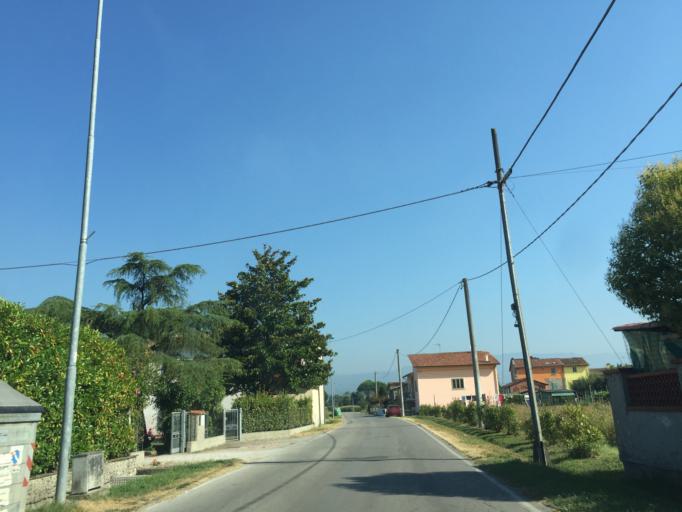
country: IT
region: Tuscany
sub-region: Provincia di Pistoia
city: Ponte Buggianese
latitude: 43.8457
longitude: 10.7432
